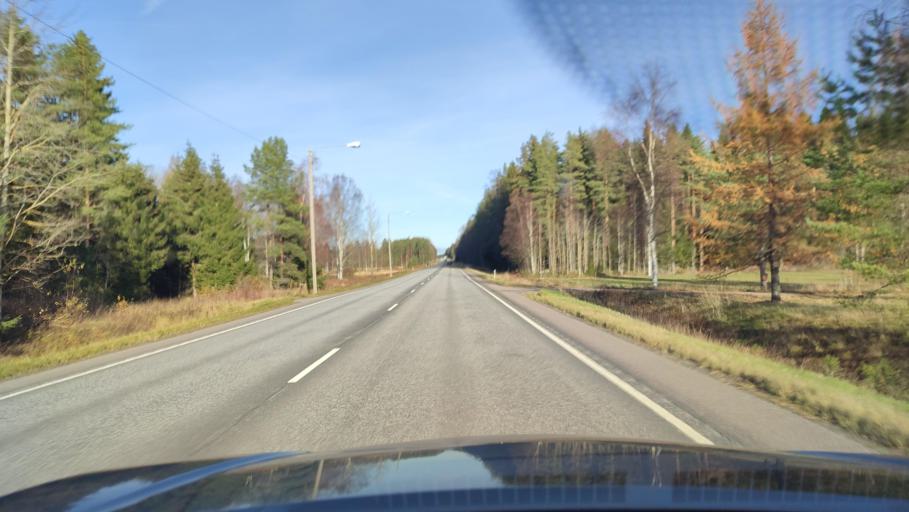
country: FI
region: Ostrobothnia
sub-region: Vaasa
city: Malax
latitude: 62.8083
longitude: 21.6810
